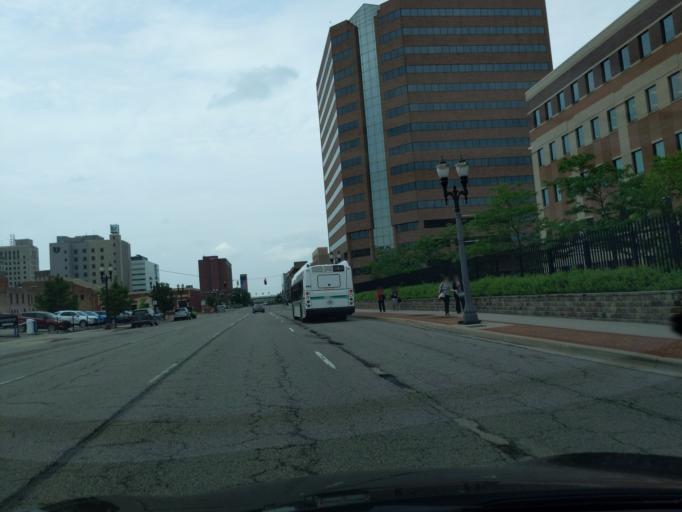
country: US
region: Michigan
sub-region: Ingham County
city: Lansing
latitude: 42.7303
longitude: -84.5507
